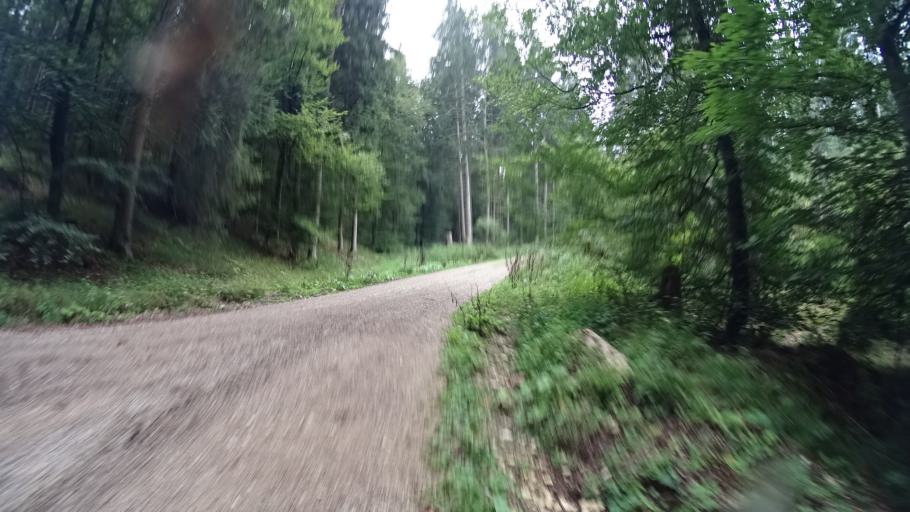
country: DE
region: Bavaria
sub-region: Upper Bavaria
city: Bohmfeld
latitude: 48.8934
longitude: 11.3502
